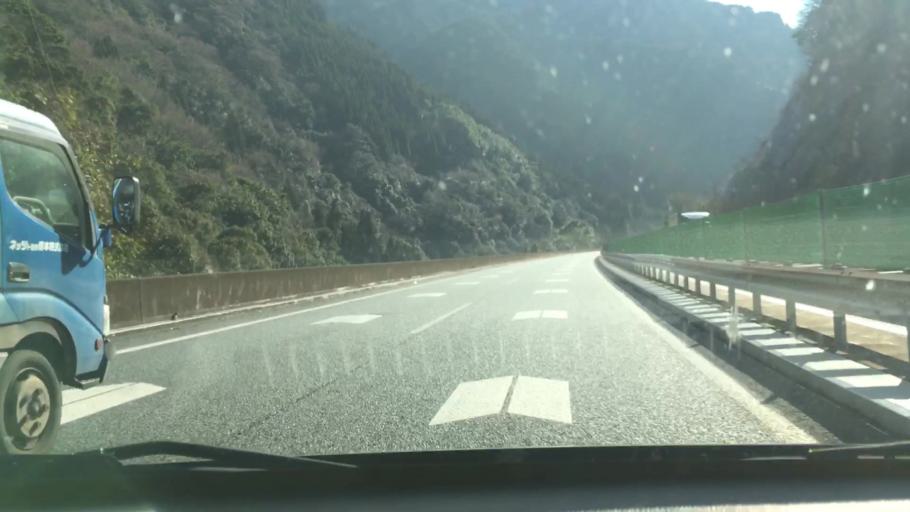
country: JP
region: Kumamoto
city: Hitoyoshi
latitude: 32.3226
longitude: 130.7580
